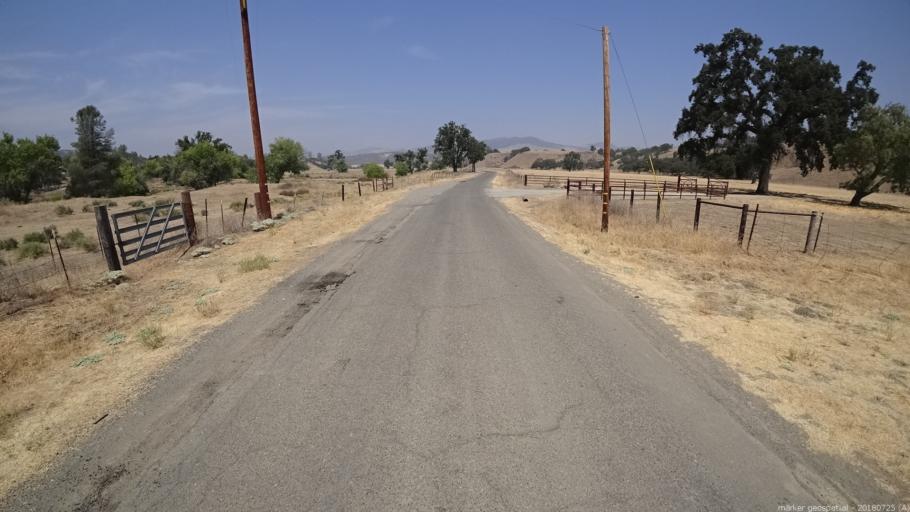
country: US
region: California
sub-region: Fresno County
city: Coalinga
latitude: 35.9065
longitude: -120.4344
